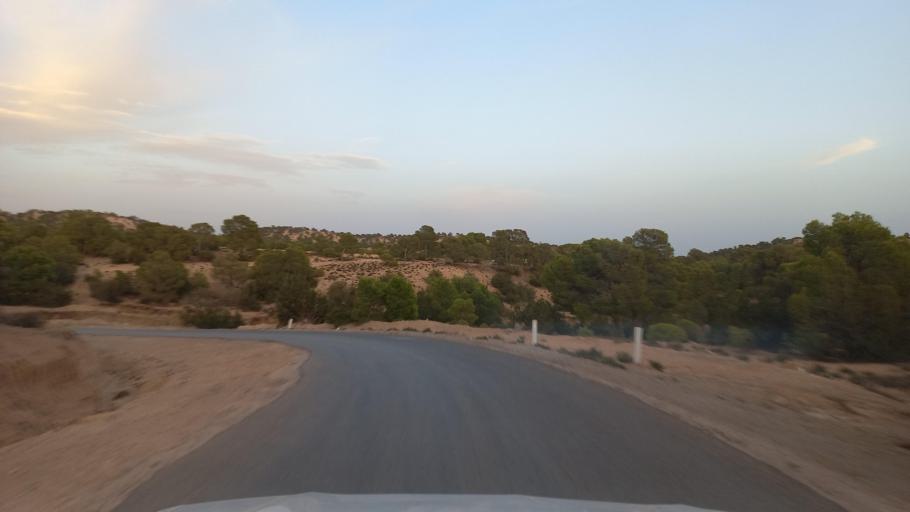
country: TN
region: Al Qasrayn
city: Sbiba
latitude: 35.4087
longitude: 8.9502
